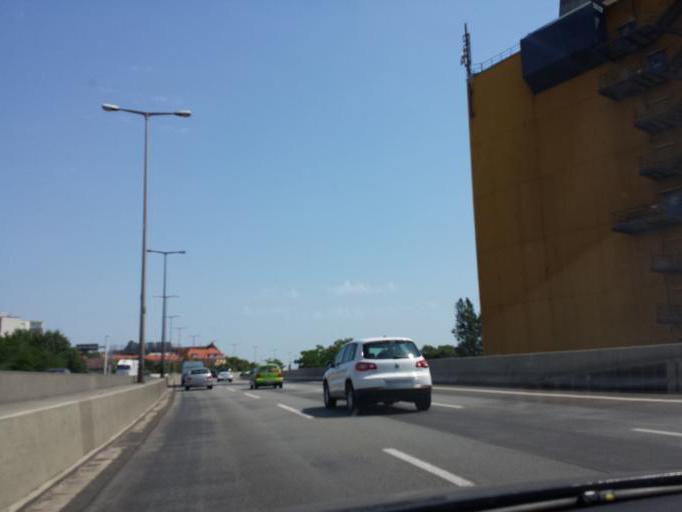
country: DE
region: Berlin
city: Wilmersdorf Bezirk
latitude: 52.4826
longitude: 13.3075
